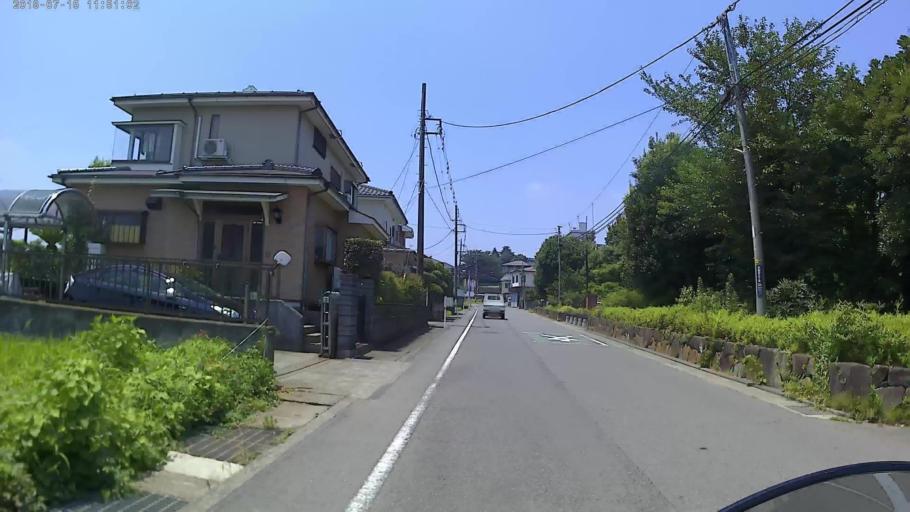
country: JP
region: Kanagawa
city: Isehara
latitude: 35.3604
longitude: 139.2807
